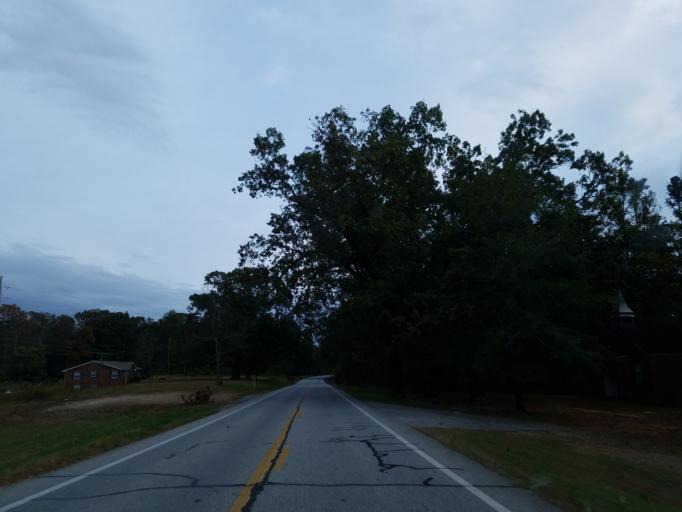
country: US
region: Georgia
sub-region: Dawson County
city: Dawsonville
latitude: 34.4648
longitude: -84.1765
